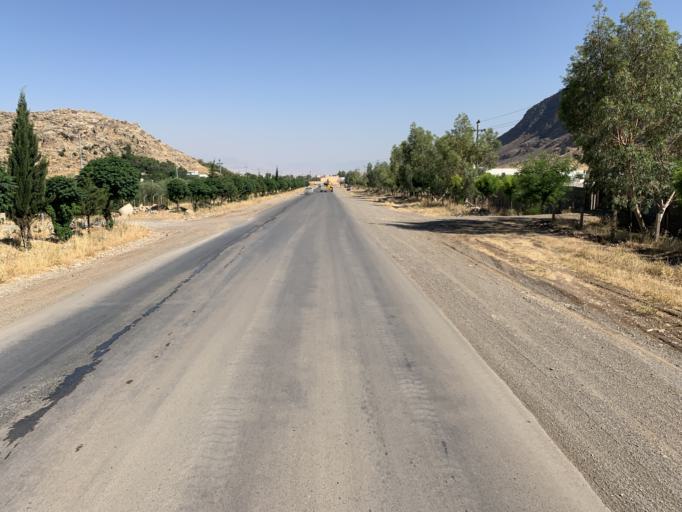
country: IQ
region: As Sulaymaniyah
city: Raniye
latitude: 36.2703
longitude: 44.8367
